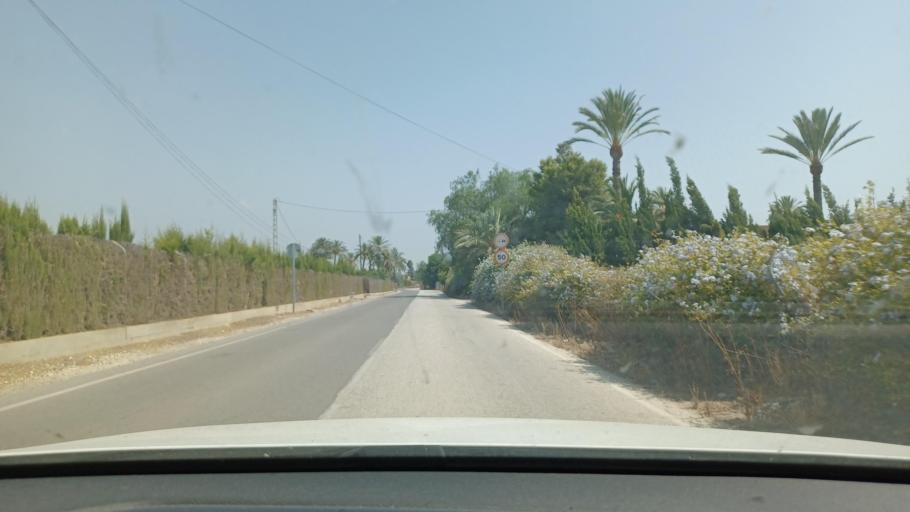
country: ES
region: Valencia
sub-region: Provincia de Alicante
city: Elche
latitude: 38.2329
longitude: -0.6934
